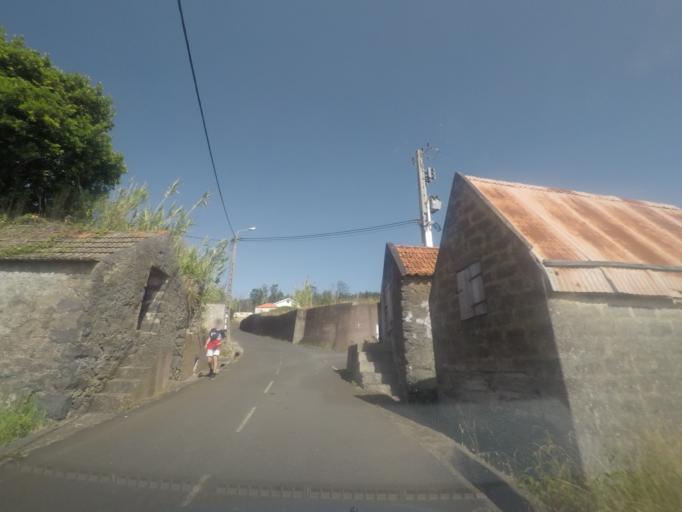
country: PT
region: Madeira
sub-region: Calheta
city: Faja da Ovelha
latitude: 32.8307
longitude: -17.2320
